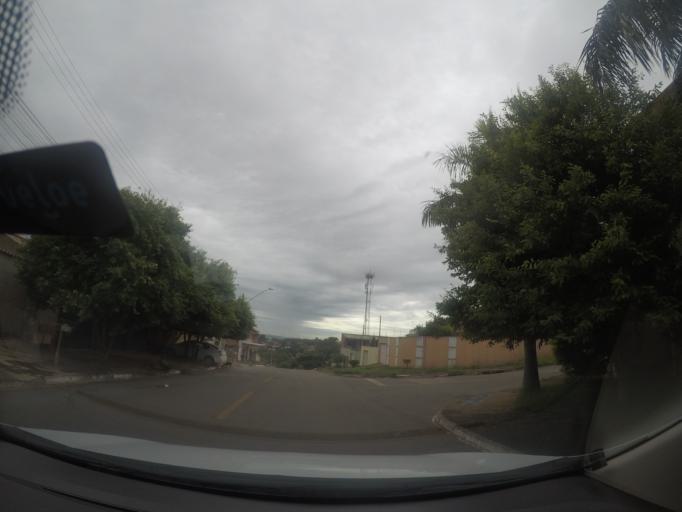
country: BR
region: Goias
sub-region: Goiania
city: Goiania
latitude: -16.6130
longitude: -49.3081
